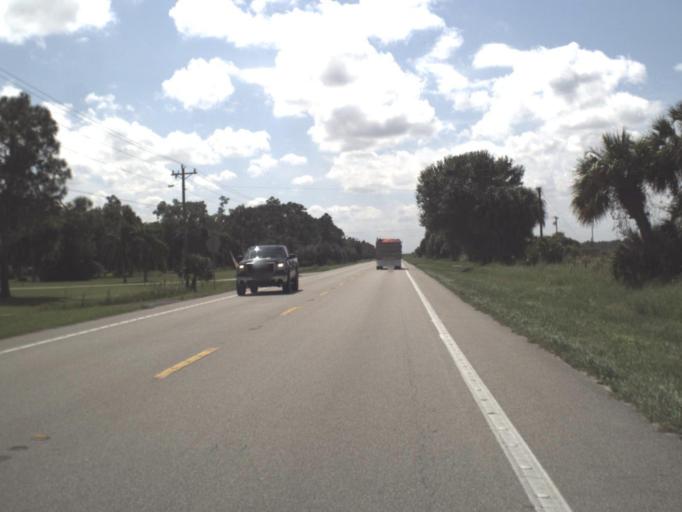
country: US
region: Florida
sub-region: Collier County
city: Immokalee
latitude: 26.5282
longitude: -81.4353
